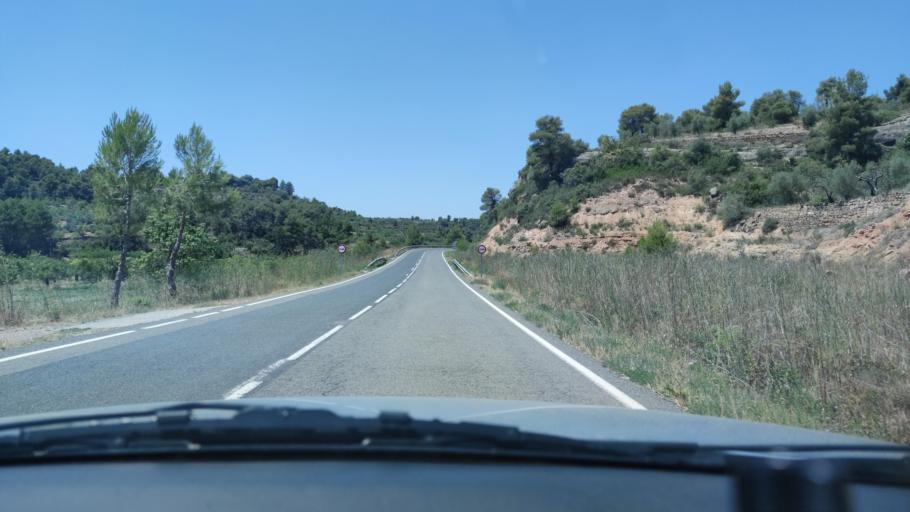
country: ES
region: Catalonia
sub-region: Provincia de Lleida
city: Juncosa
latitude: 41.3777
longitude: 0.7559
